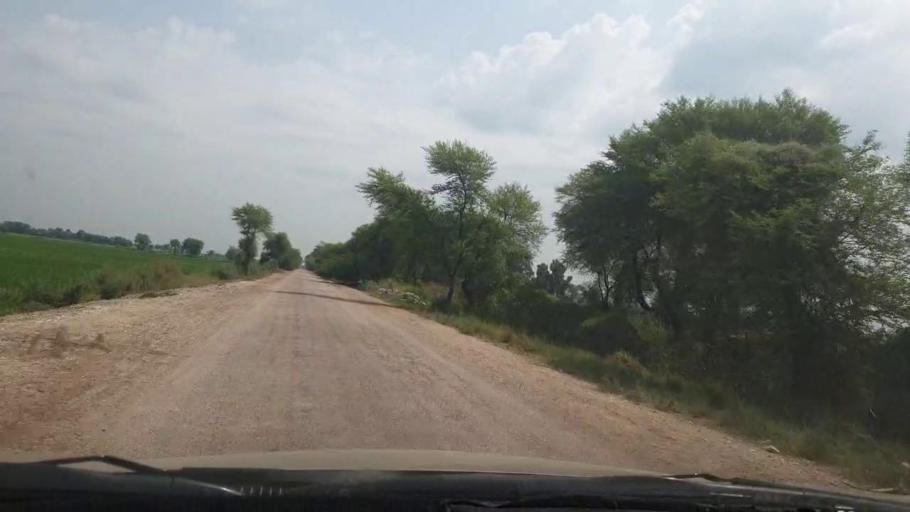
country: PK
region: Sindh
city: Miro Khan
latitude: 27.6898
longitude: 68.1942
